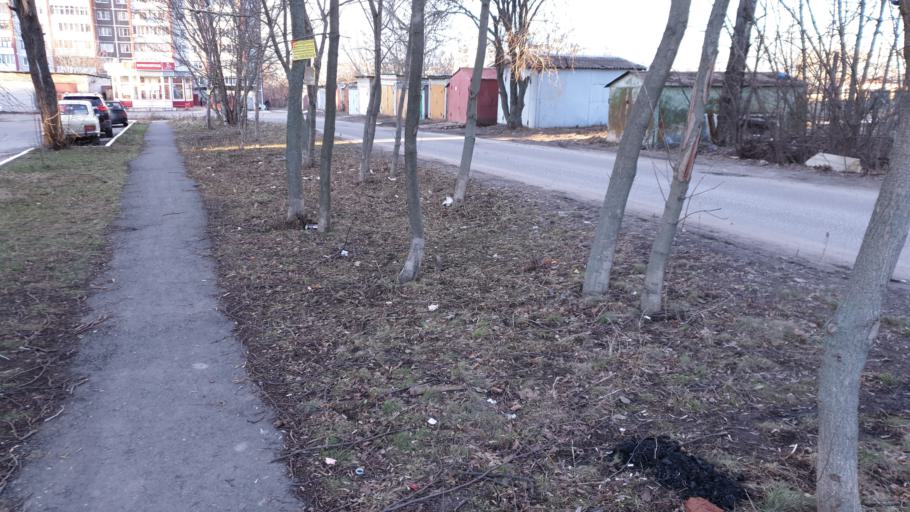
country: RU
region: Kursk
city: Kursk
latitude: 51.7262
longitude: 36.1500
